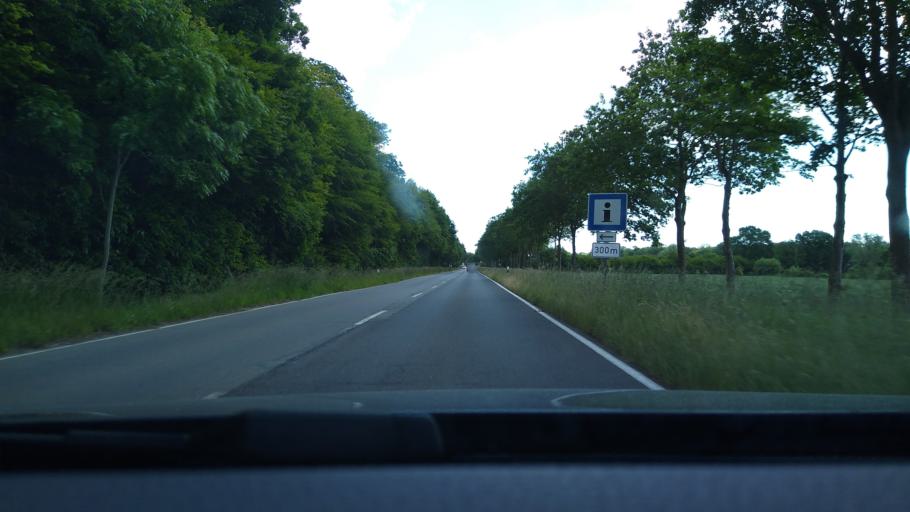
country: DE
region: Schleswig-Holstein
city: Dahme
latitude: 54.2136
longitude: 11.0633
